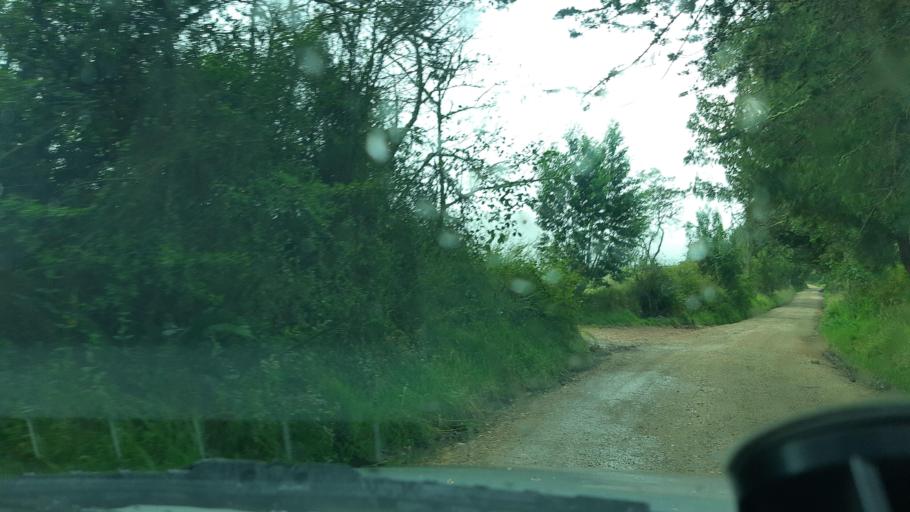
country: CO
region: Cundinamarca
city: Villapinzon
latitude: 5.2233
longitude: -73.5760
